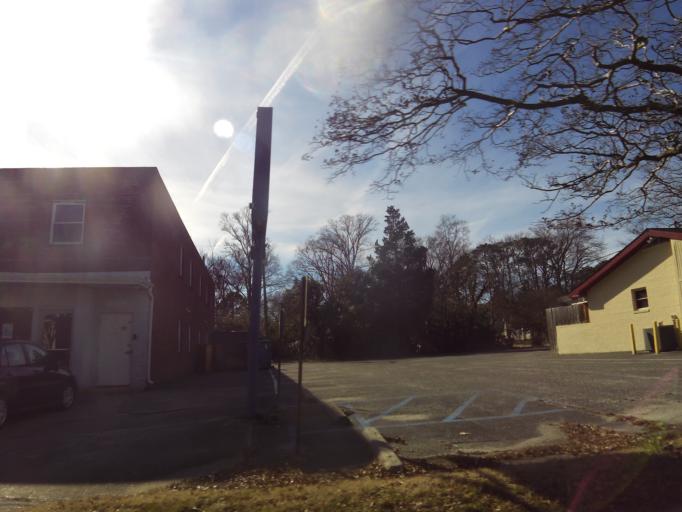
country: US
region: Virginia
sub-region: City of Newport News
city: Newport News
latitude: 37.0339
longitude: -76.4630
